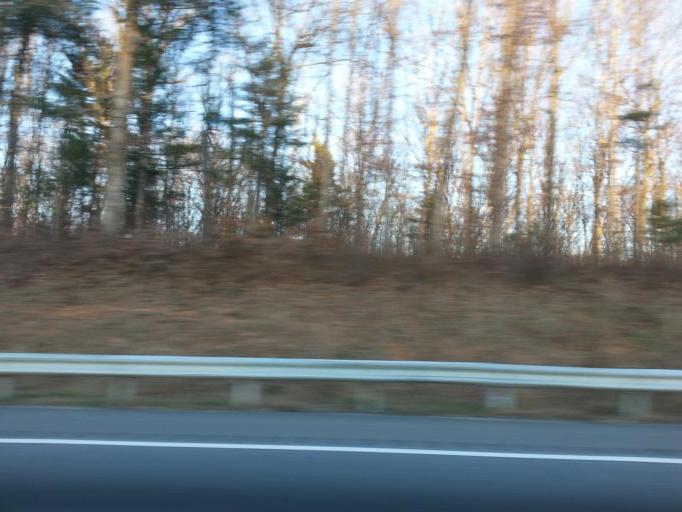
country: US
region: North Carolina
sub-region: Buncombe County
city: Bent Creek
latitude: 35.5329
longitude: -82.6018
